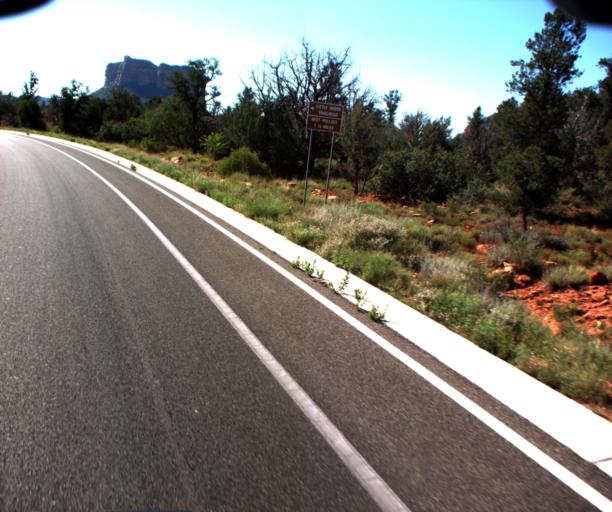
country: US
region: Arizona
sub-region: Yavapai County
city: Village of Oak Creek (Big Park)
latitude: 34.8237
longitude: -111.7773
